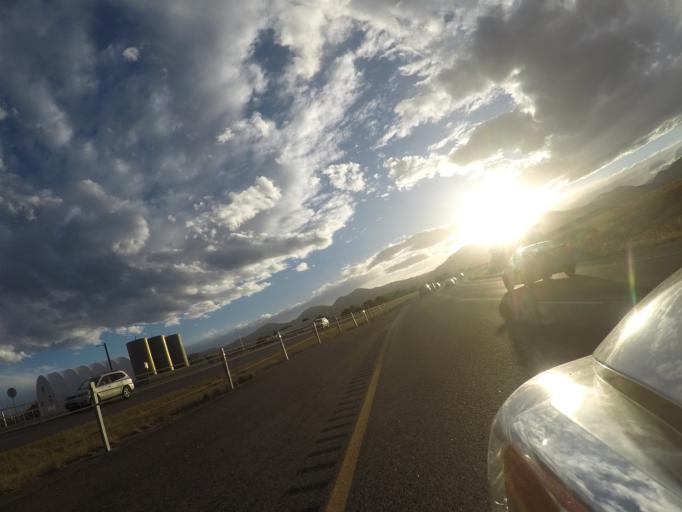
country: US
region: Colorado
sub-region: Jefferson County
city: Ken Caryl
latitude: 39.6398
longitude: -105.1379
